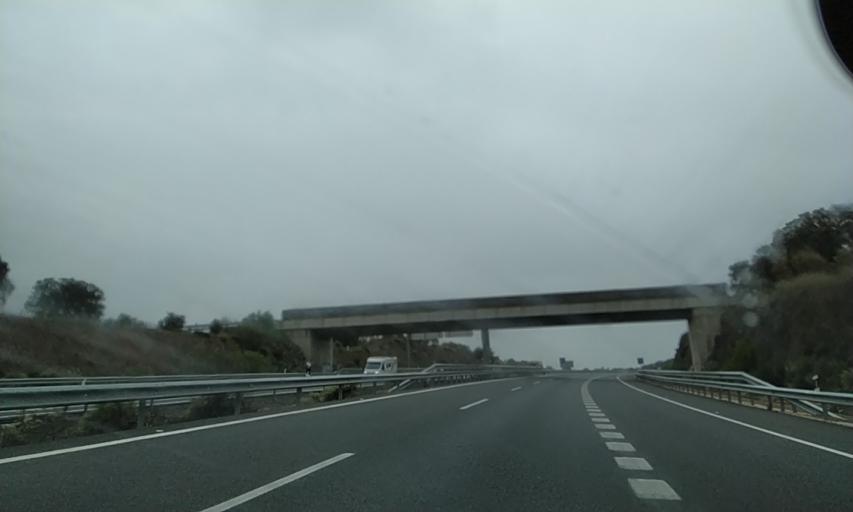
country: ES
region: Extremadura
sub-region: Provincia de Caceres
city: Plasencia
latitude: 40.0301
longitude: -6.1209
